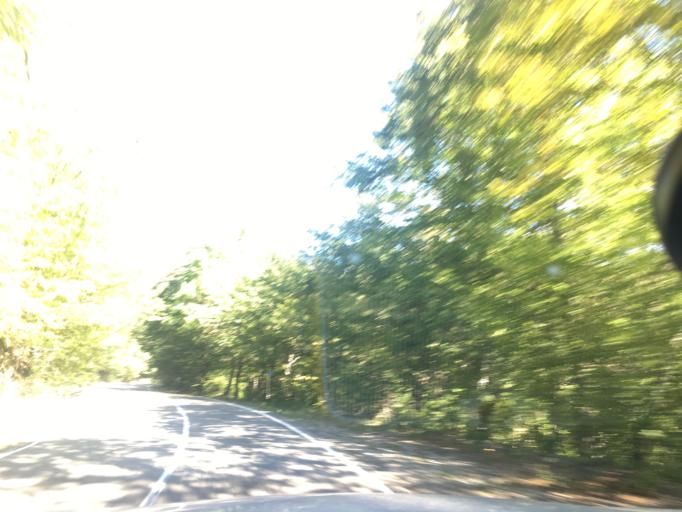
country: GE
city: Didi Lilo
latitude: 41.8641
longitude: 44.9143
